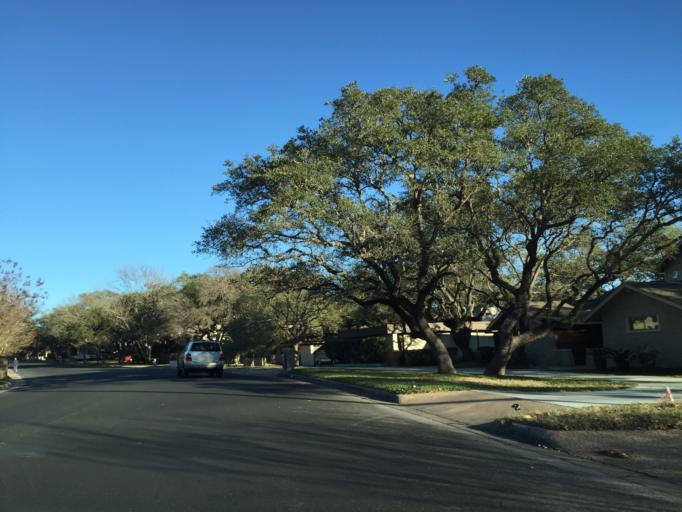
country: US
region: Texas
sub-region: Williamson County
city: Jollyville
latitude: 30.4381
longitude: -97.7891
